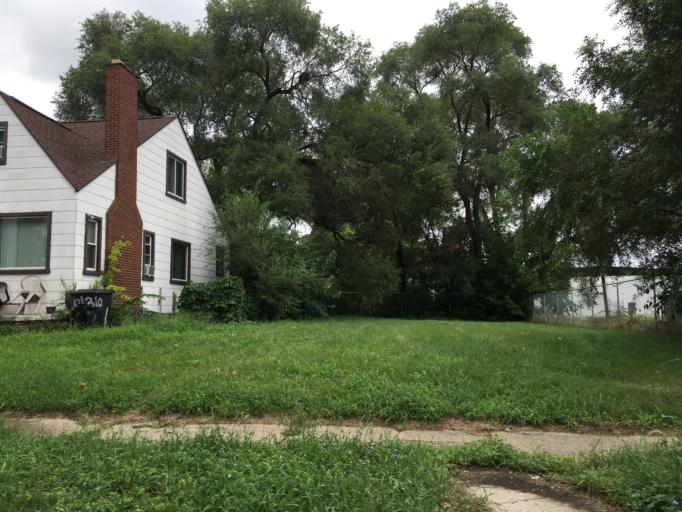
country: US
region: Michigan
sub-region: Wayne County
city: Highland Park
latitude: 42.4104
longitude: -83.1438
